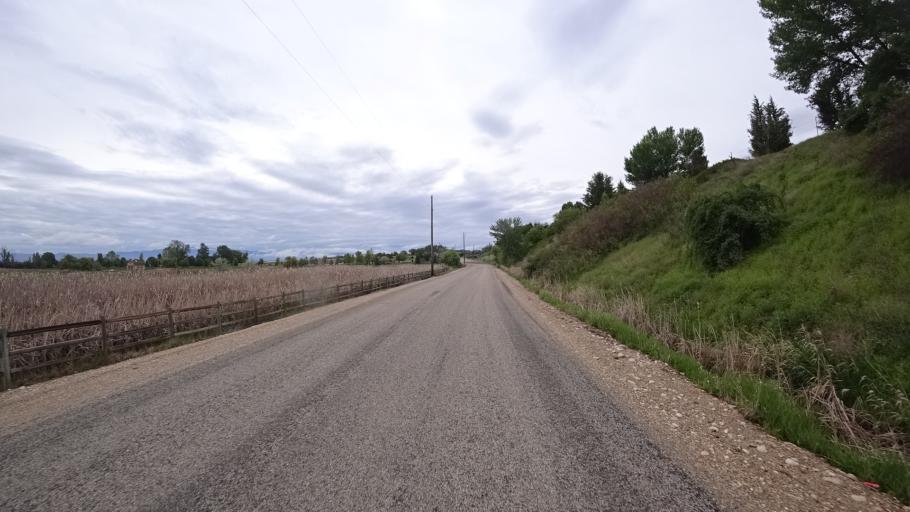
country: US
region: Idaho
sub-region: Ada County
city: Star
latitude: 43.6702
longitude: -116.4763
